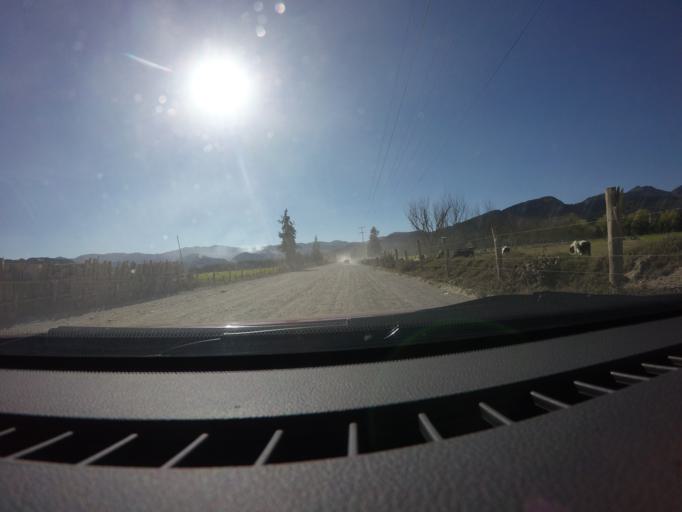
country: CO
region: Cundinamarca
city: Ubate
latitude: 5.2749
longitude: -73.8001
